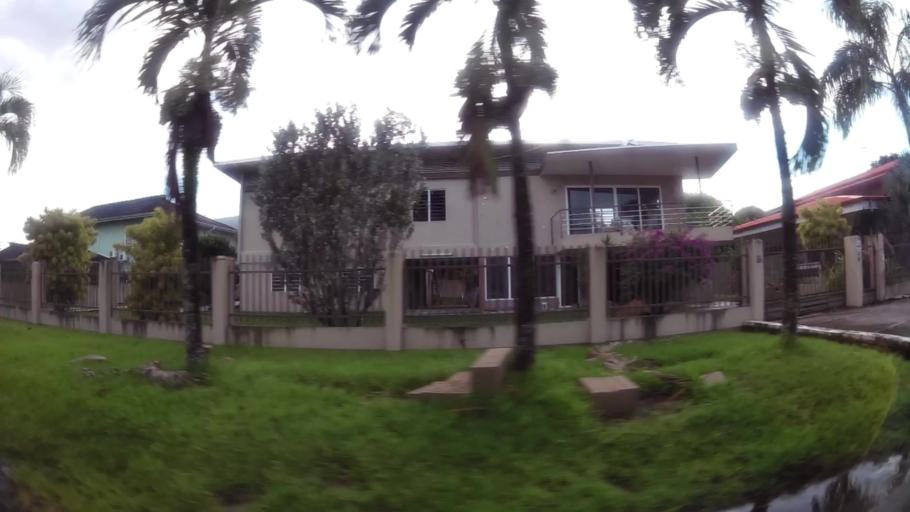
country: SR
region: Paramaribo
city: Paramaribo
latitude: 5.8318
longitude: -55.1842
